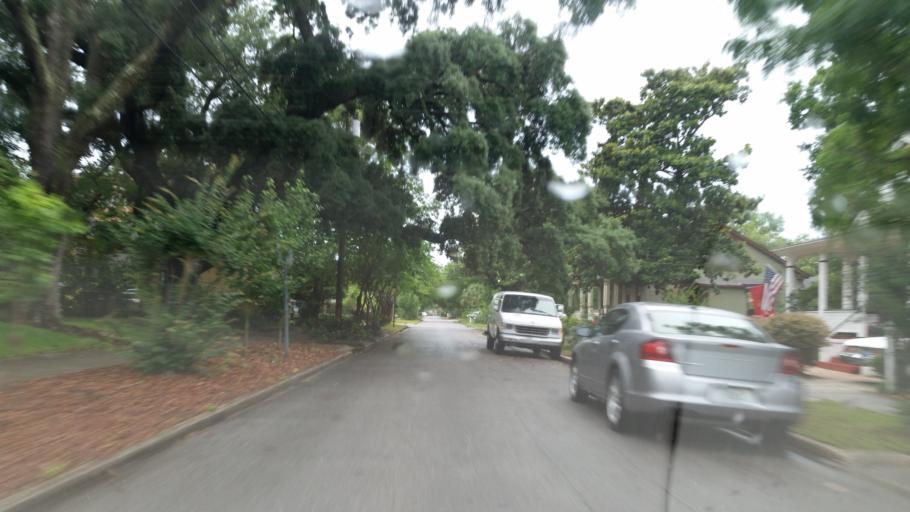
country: US
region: Florida
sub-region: Escambia County
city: Pensacola
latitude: 30.4208
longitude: -87.2088
